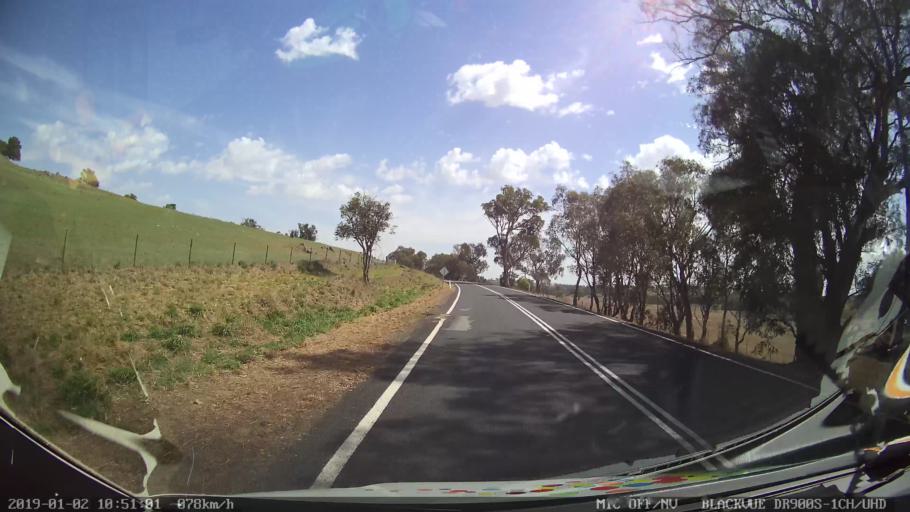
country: AU
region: New South Wales
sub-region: Cootamundra
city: Cootamundra
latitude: -34.7057
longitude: 148.2756
